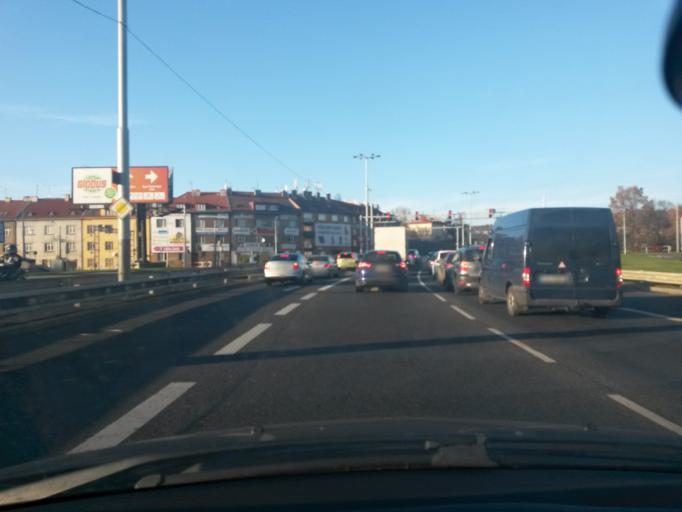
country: CZ
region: Praha
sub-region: Praha 9
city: Vysocany
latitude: 50.1041
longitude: 14.5316
